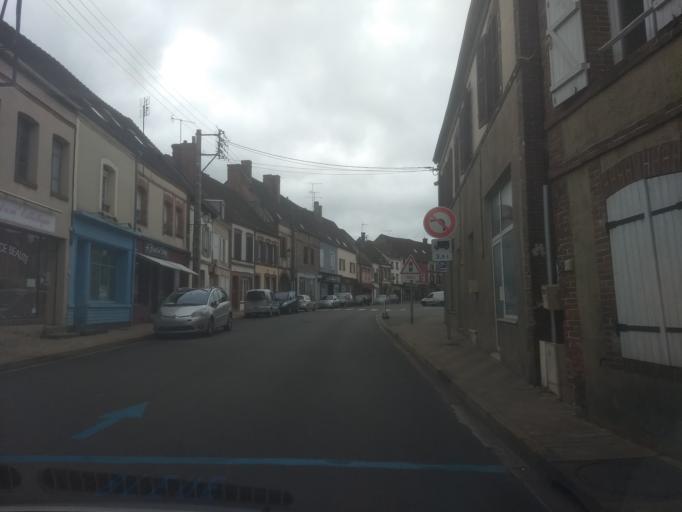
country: FR
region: Centre
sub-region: Departement d'Eure-et-Loir
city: Chateauneuf-en-Thymerais
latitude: 48.5820
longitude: 1.2425
